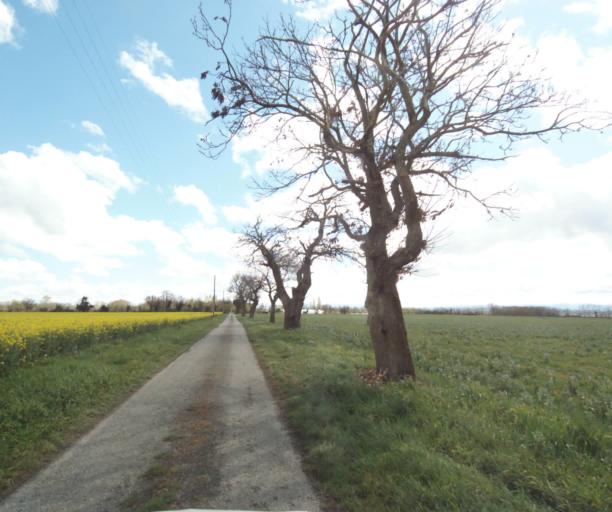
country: FR
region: Midi-Pyrenees
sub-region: Departement de l'Ariege
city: Saverdun
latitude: 43.2639
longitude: 1.5948
